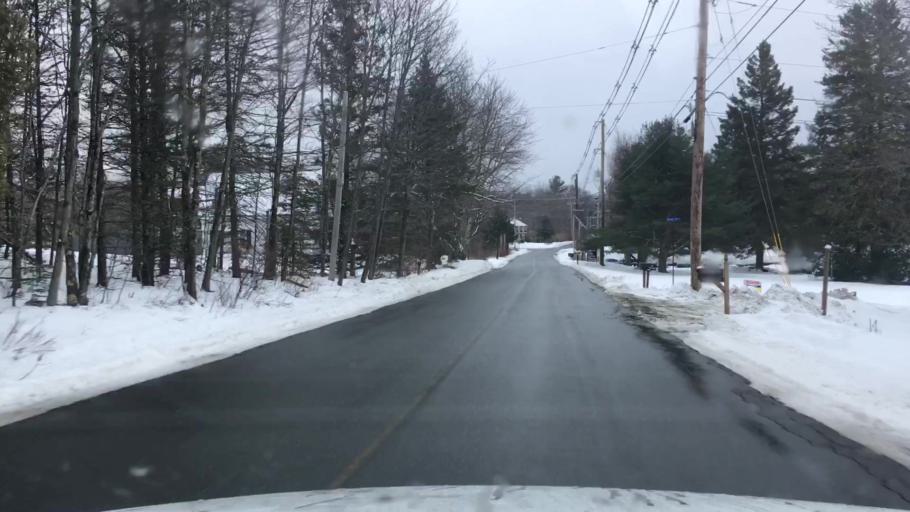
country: US
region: Maine
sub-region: Hancock County
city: Trenton
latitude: 44.4132
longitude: -68.3345
